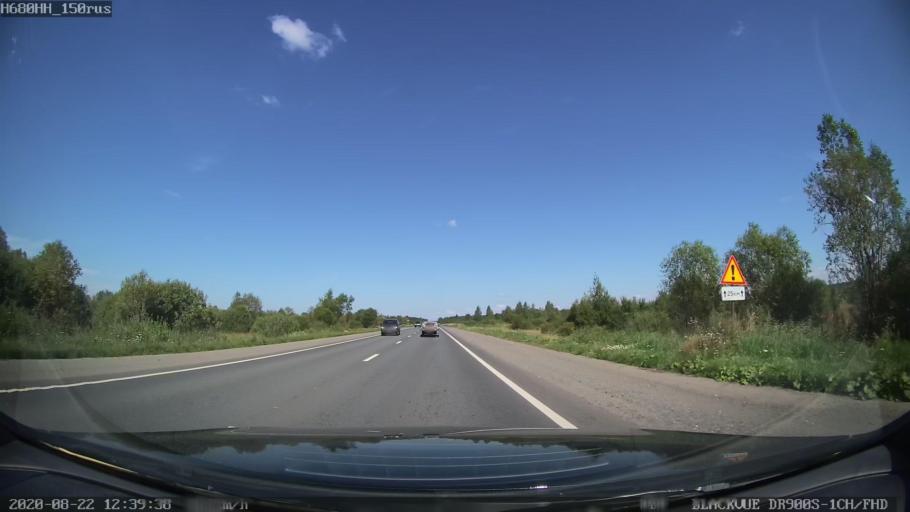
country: RU
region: Tverskaya
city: Rameshki
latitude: 57.3337
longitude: 36.0942
